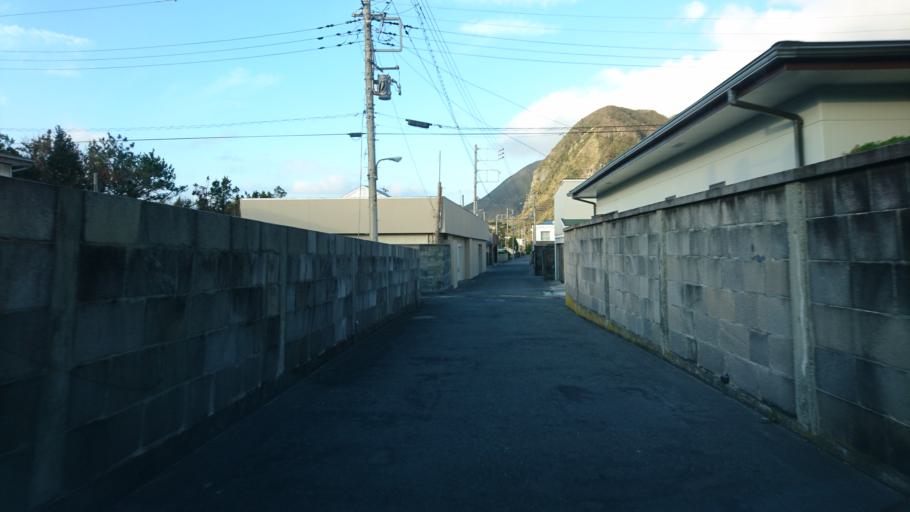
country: JP
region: Shizuoka
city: Shimoda
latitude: 34.3783
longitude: 139.2546
